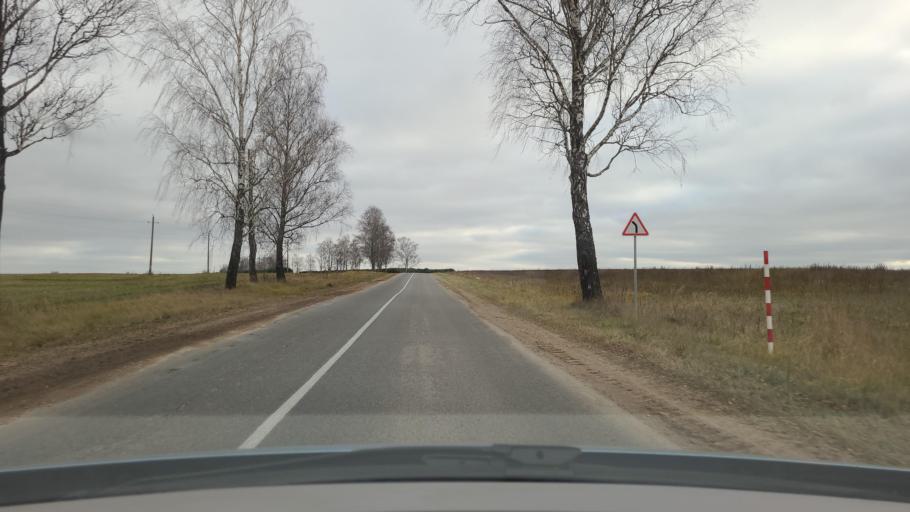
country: BY
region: Minsk
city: Khalopyenichy
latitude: 54.4764
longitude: 28.9608
